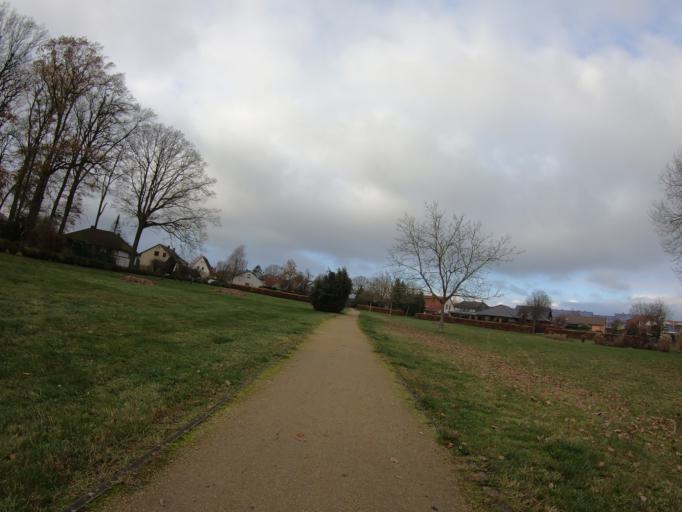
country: DE
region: Lower Saxony
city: Wesendorf
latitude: 52.5888
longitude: 10.5364
